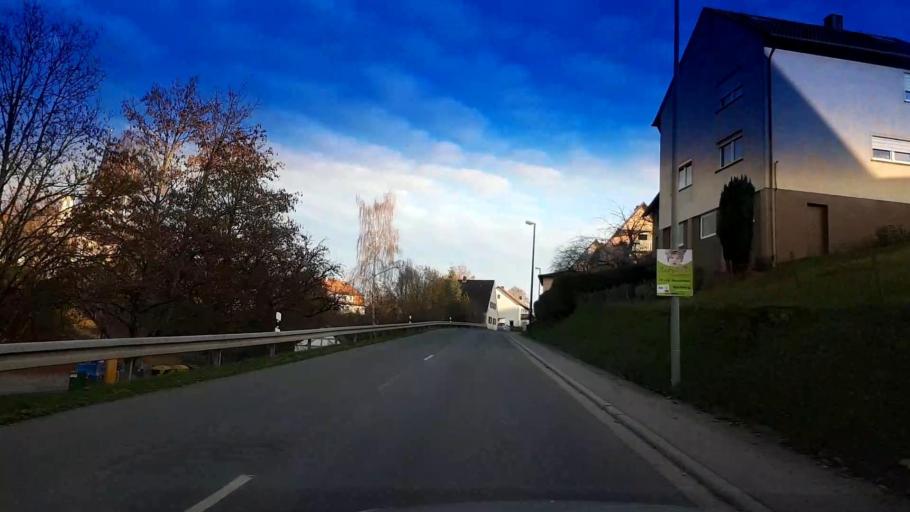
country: DE
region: Bavaria
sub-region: Upper Franconia
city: Priesendorf
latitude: 49.8831
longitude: 10.7261
